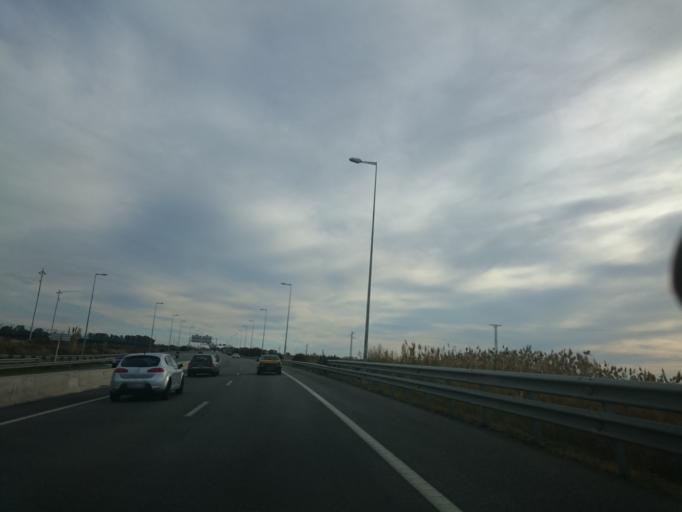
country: ES
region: Catalonia
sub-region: Provincia de Barcelona
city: Viladecans
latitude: 41.2940
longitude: 2.0503
